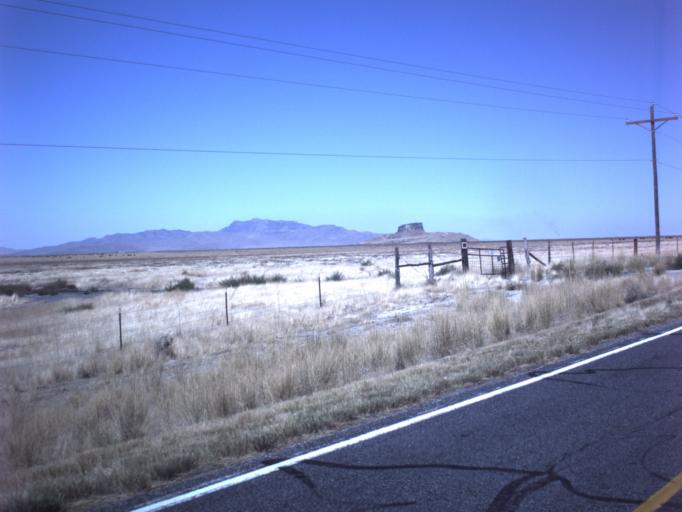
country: US
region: Utah
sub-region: Tooele County
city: Grantsville
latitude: 40.6818
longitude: -112.6709
